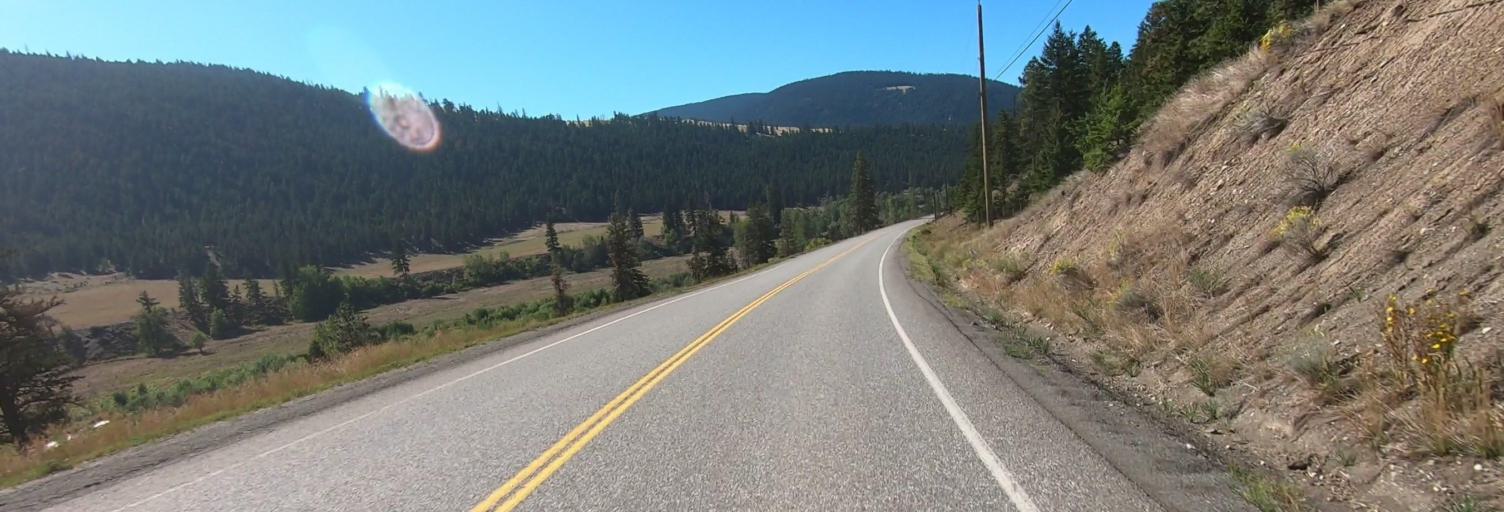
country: CA
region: British Columbia
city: Cache Creek
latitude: 50.8435
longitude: -121.5409
